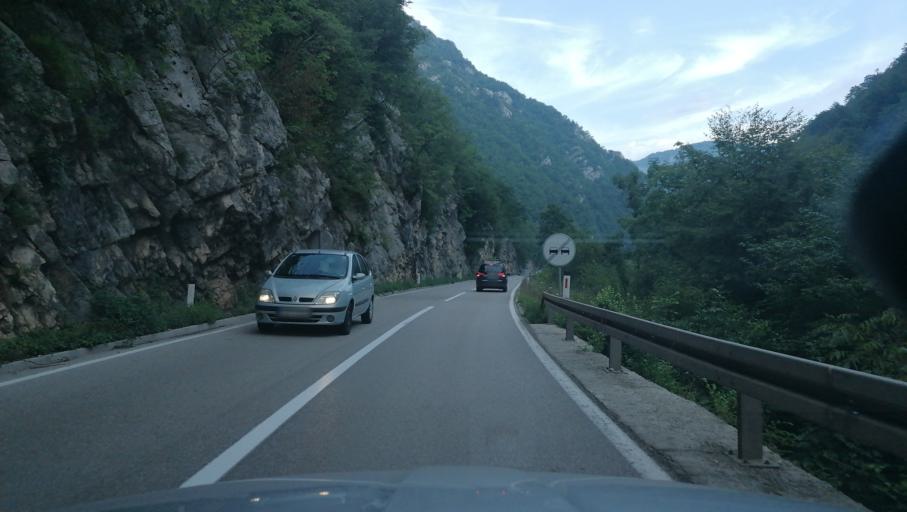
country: BA
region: Federation of Bosnia and Herzegovina
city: Jajce
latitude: 44.4375
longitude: 17.2344
